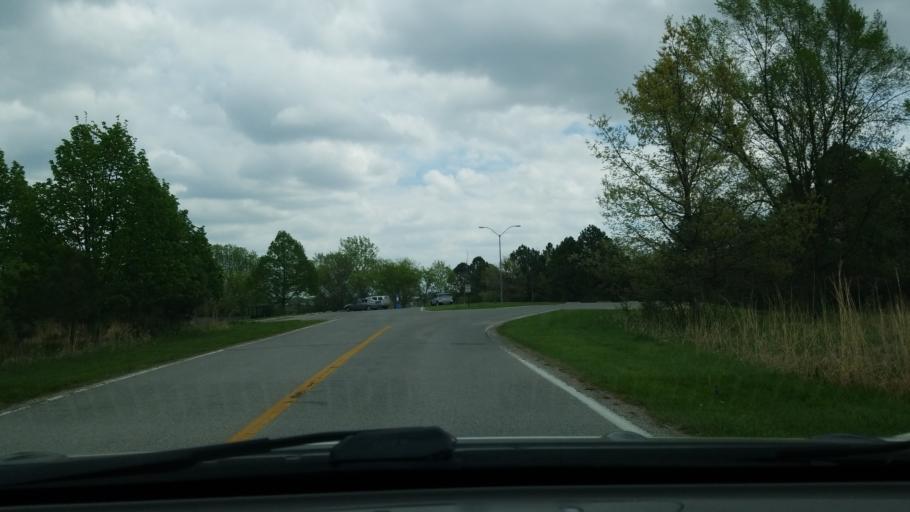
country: US
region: Nebraska
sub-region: Sarpy County
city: Chalco
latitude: 41.1656
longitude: -96.1608
